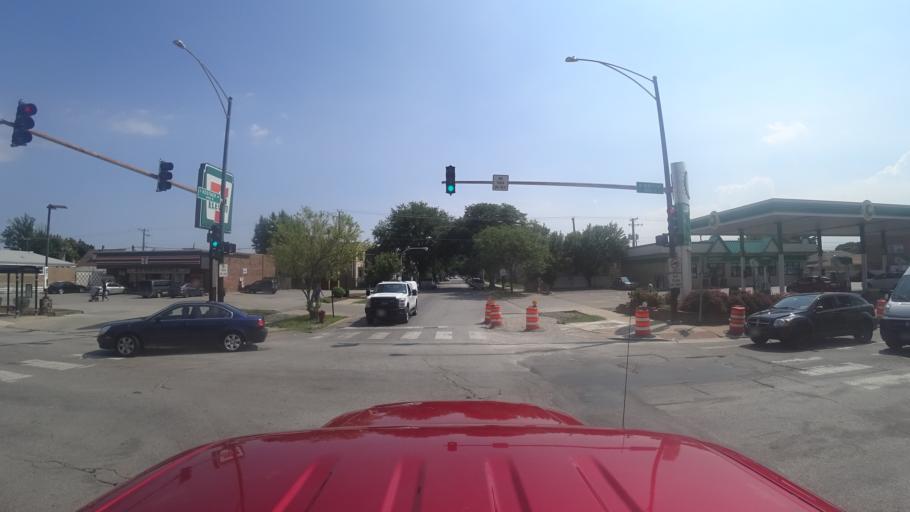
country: US
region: Illinois
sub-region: Cook County
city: Cicero
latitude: 41.7932
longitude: -87.7330
